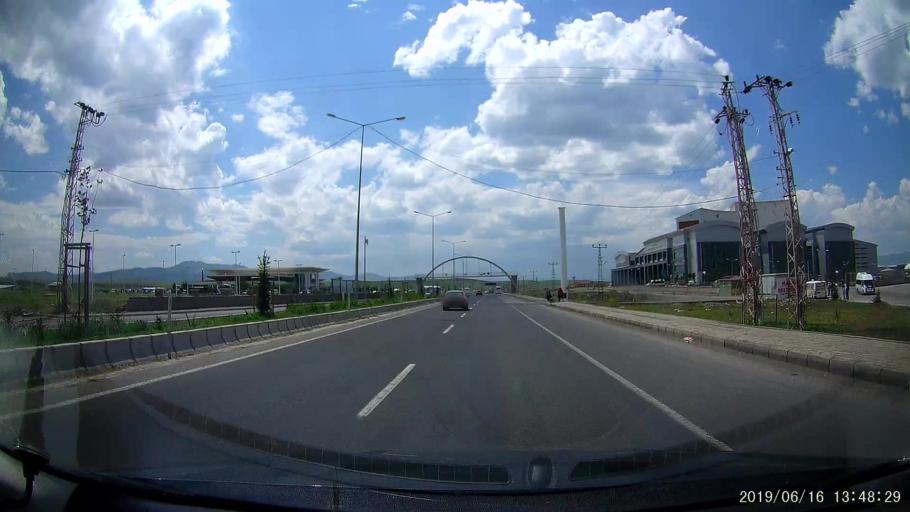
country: TR
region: Agri
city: Agri
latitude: 39.7145
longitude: 43.0059
